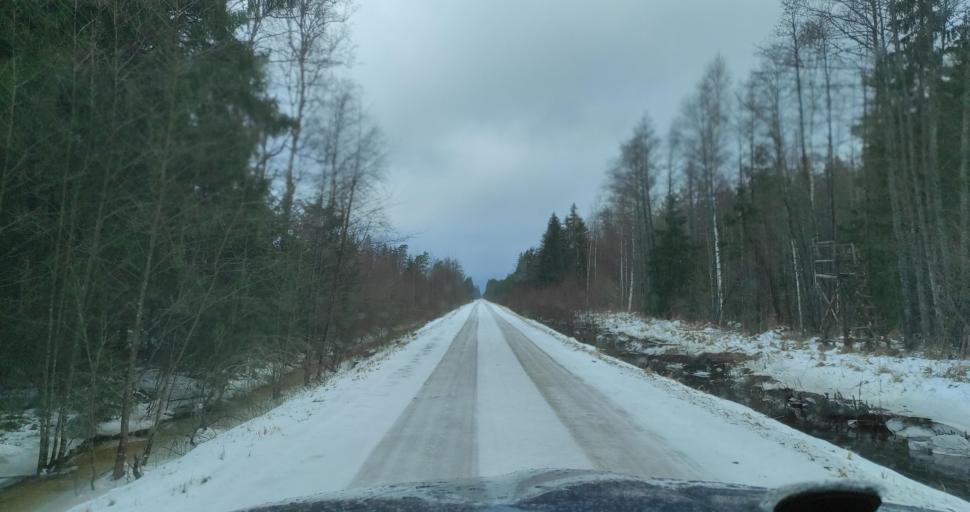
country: LV
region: Dundaga
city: Dundaga
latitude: 57.3978
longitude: 22.1143
